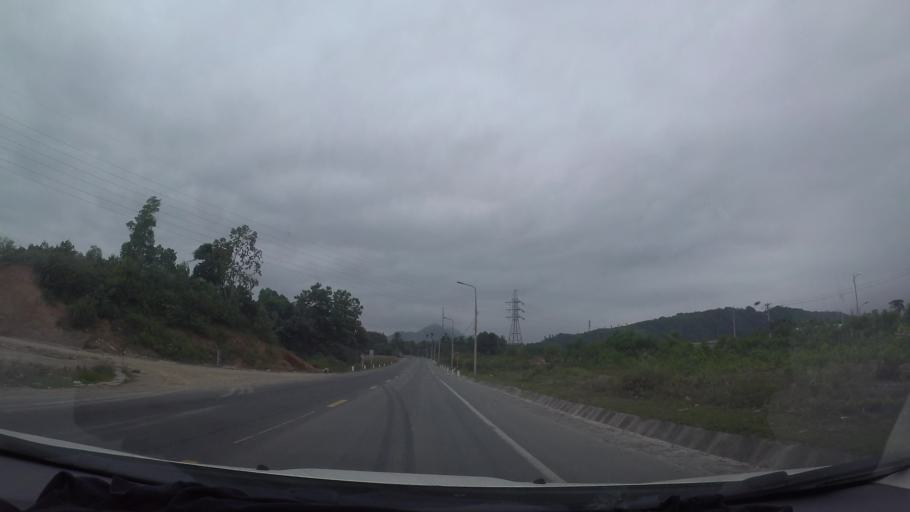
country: VN
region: Da Nang
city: Lien Chieu
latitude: 16.0829
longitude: 108.0847
